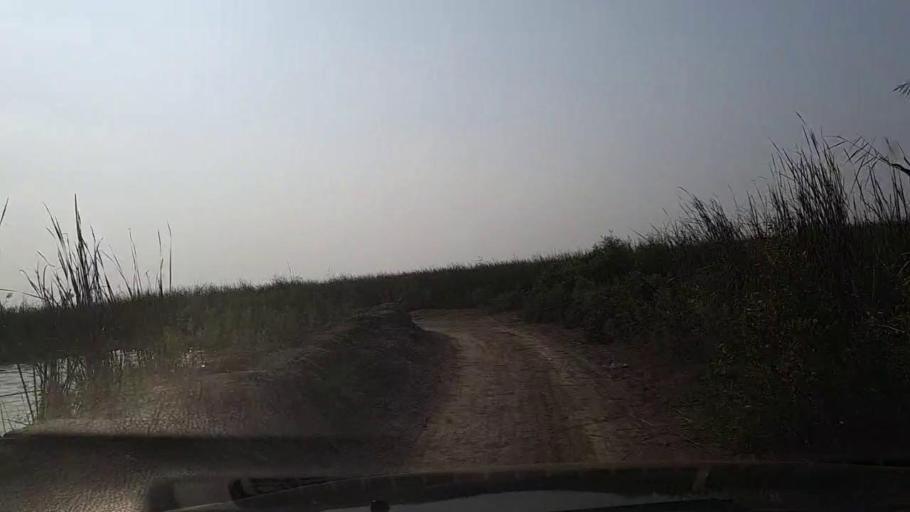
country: PK
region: Sindh
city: Mirpur Batoro
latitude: 24.6474
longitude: 68.2829
